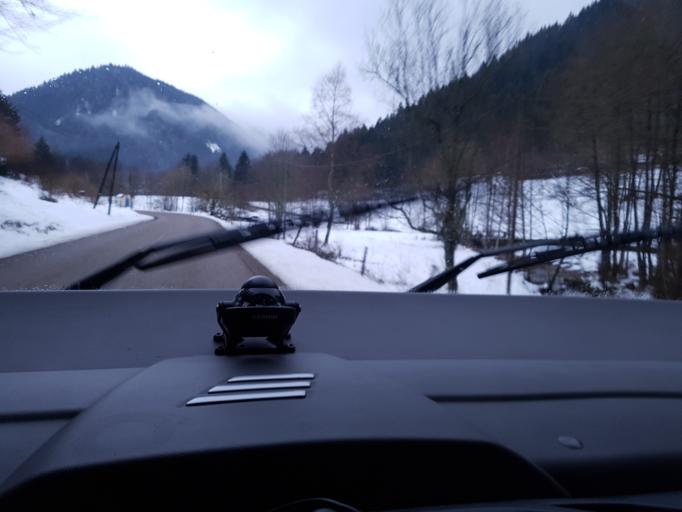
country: FR
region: Lorraine
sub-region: Departement des Vosges
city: Plainfaing
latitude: 48.1308
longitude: 7.0282
